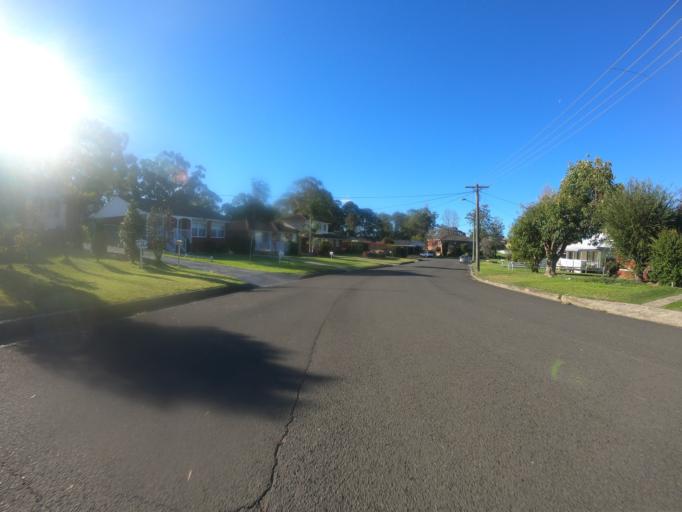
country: AU
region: New South Wales
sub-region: Wollongong
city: Cordeaux Heights
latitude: -34.4562
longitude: 150.8401
